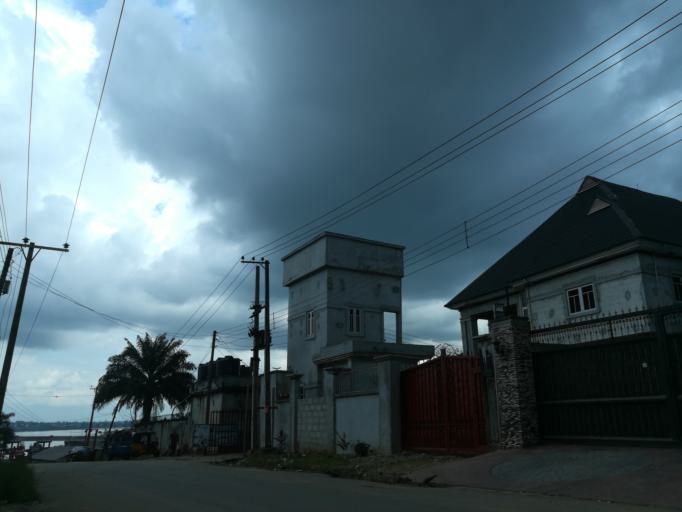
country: NG
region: Rivers
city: Port Harcourt
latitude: 4.8170
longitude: 7.0695
